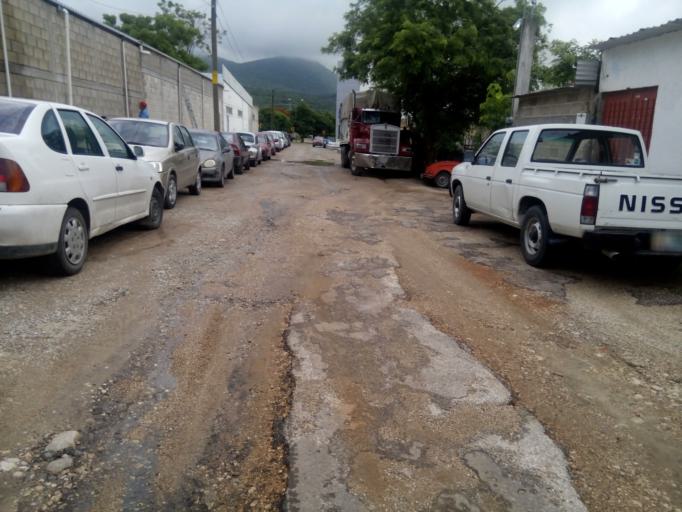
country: MX
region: Chiapas
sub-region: San Fernando
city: Alvaro Obregon
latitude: 16.7697
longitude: -93.1939
